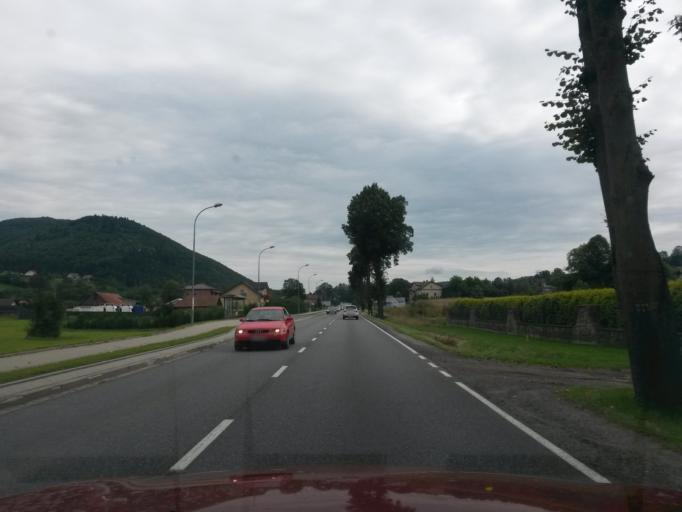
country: PL
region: Lesser Poland Voivodeship
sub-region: Powiat nowosadecki
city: Nawojowa
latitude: 49.5539
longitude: 20.7587
